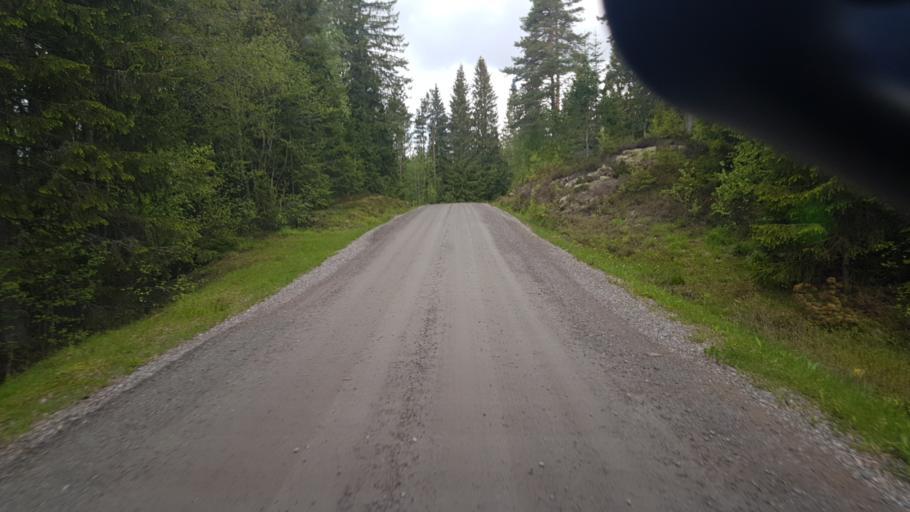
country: NO
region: Ostfold
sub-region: Romskog
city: Romskog
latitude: 59.7110
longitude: 12.0318
